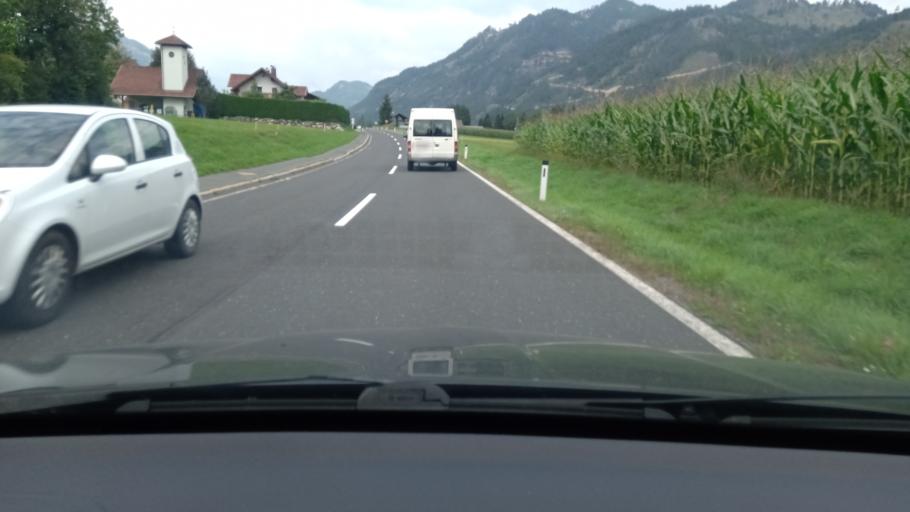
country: AT
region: Carinthia
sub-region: Politischer Bezirk Hermagor
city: Hermagor
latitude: 46.6611
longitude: 13.3118
